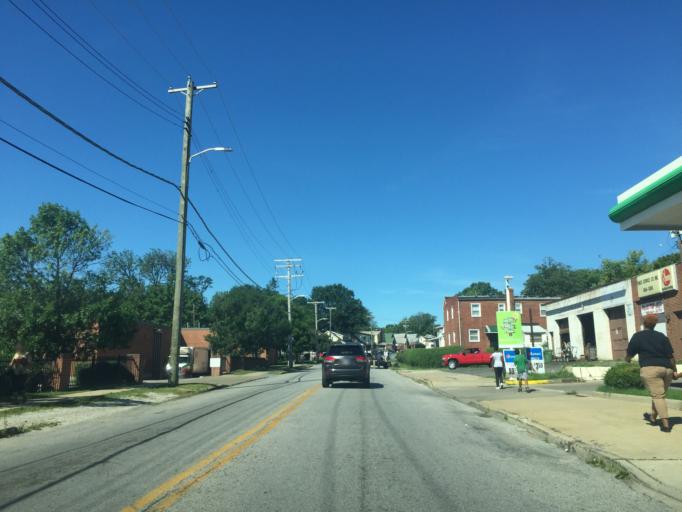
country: US
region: Maryland
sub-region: Baltimore County
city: Lochearn
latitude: 39.3360
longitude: -76.6756
